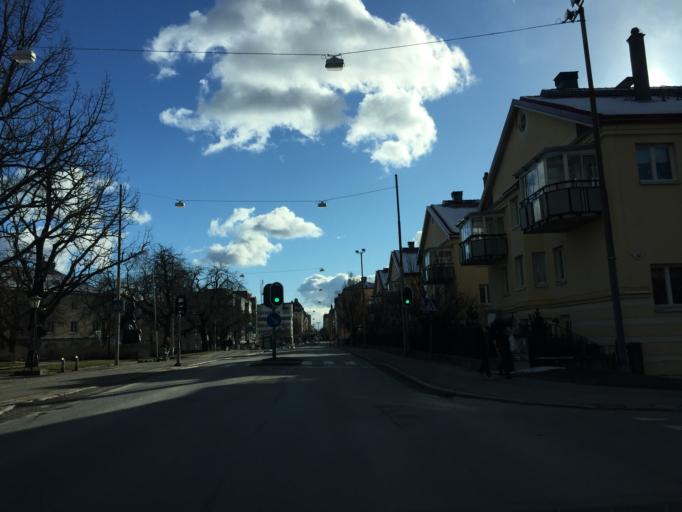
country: SE
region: OErebro
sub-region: Orebro Kommun
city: Orebro
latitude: 59.2806
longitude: 15.2188
